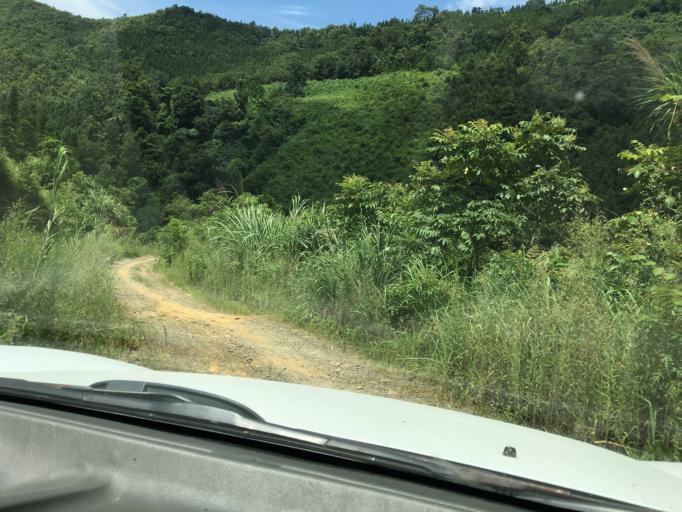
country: CN
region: Guangxi Zhuangzu Zizhiqu
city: Tongle
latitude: 24.9714
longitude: 105.9851
